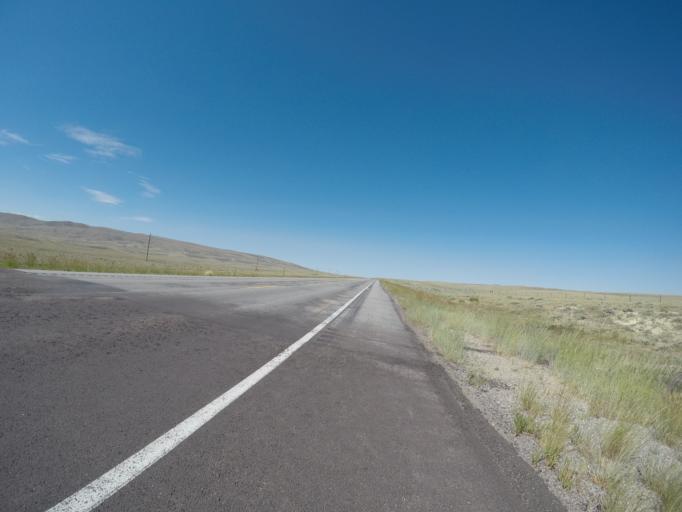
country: US
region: Wyoming
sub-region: Carbon County
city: Saratoga
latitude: 41.8030
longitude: -106.7035
